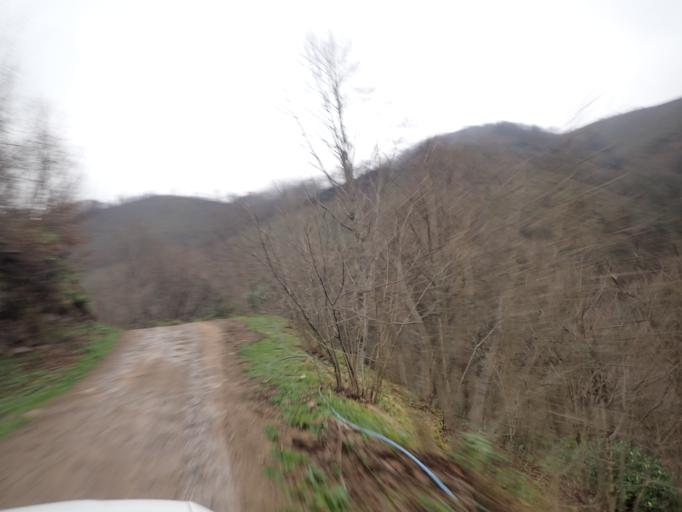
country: TR
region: Ordu
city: Camas
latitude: 40.8620
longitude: 37.5072
